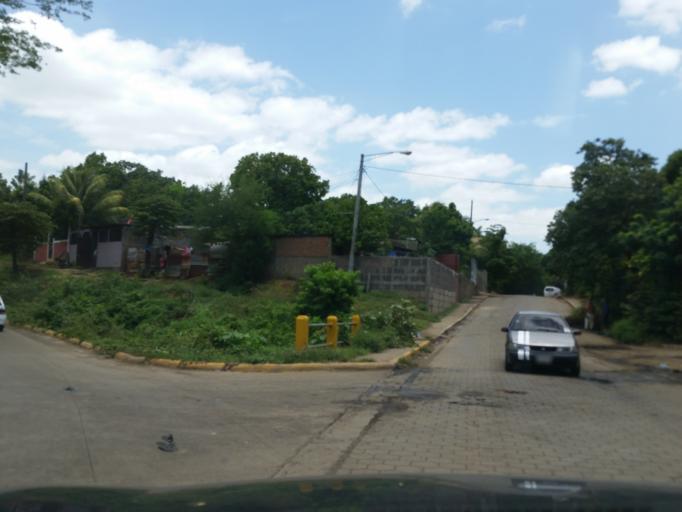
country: NI
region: Managua
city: Managua
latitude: 12.1069
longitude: -86.2389
